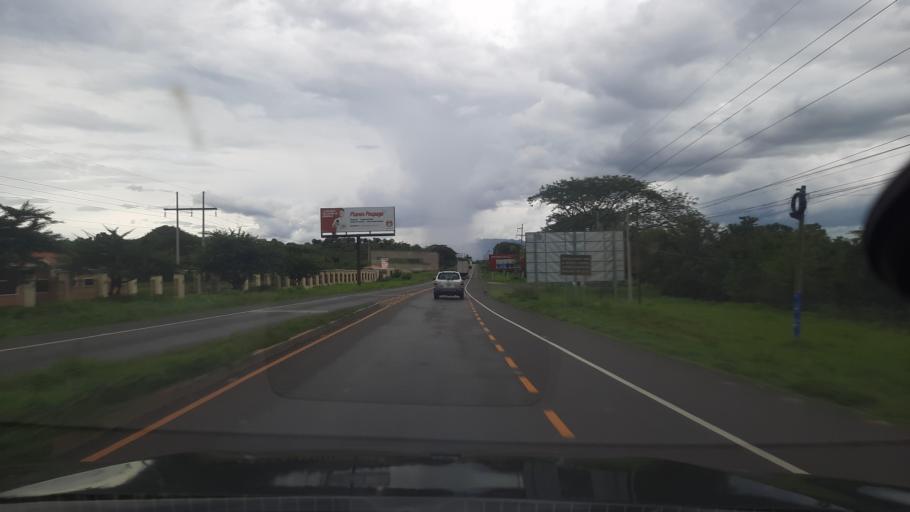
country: HN
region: Choluteca
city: Ciudad Choluteca
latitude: 13.3427
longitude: -87.2521
